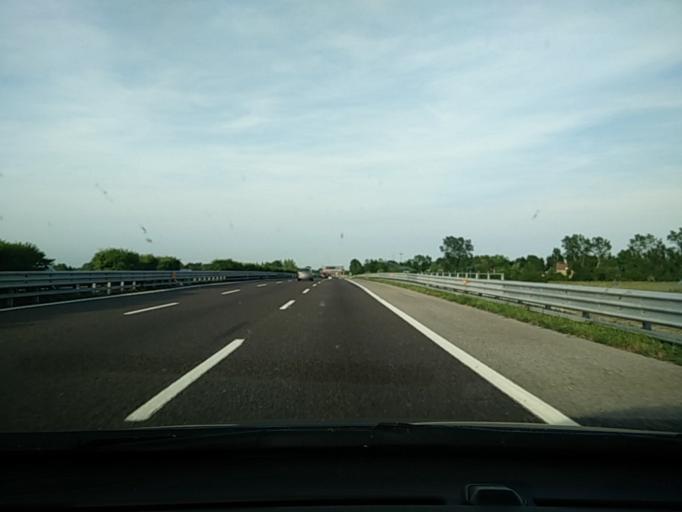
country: IT
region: Veneto
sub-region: Provincia di Venezia
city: Marano
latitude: 45.4585
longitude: 12.1349
